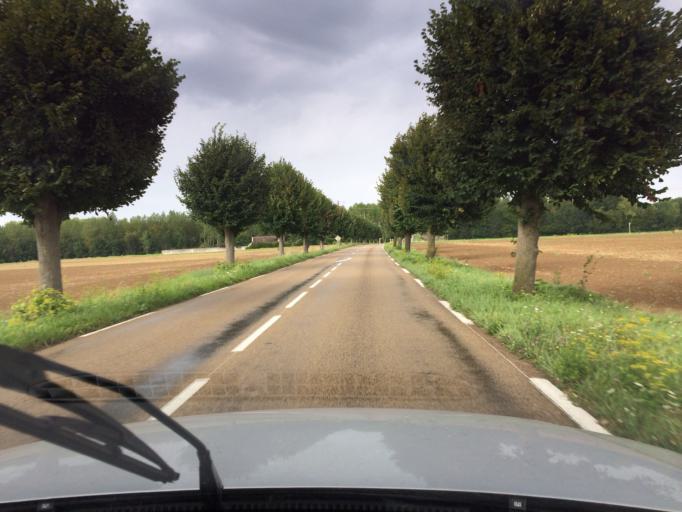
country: FR
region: Bourgogne
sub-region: Departement de l'Yonne
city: Joigny
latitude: 47.9618
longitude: 3.3814
